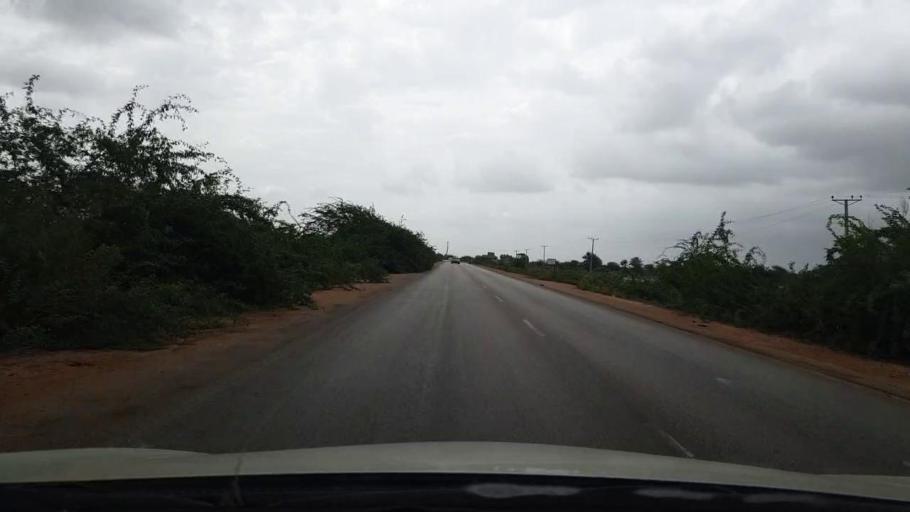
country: PK
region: Sindh
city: Mirpur Batoro
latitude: 24.6161
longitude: 68.2771
